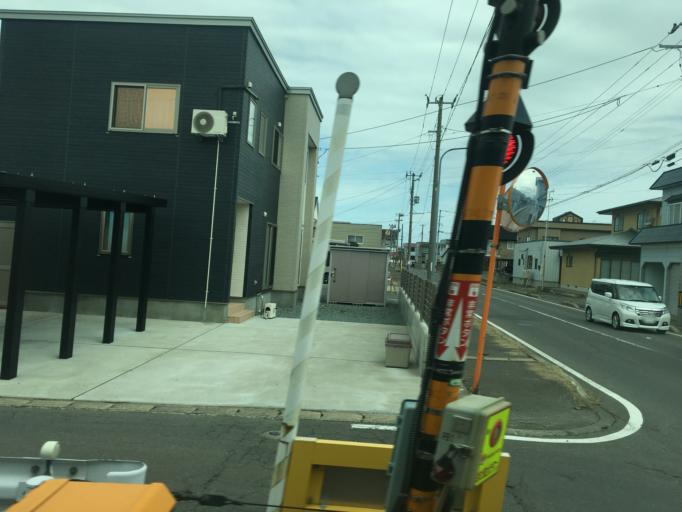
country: JP
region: Aomori
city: Hirosaki
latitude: 40.6522
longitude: 140.5017
